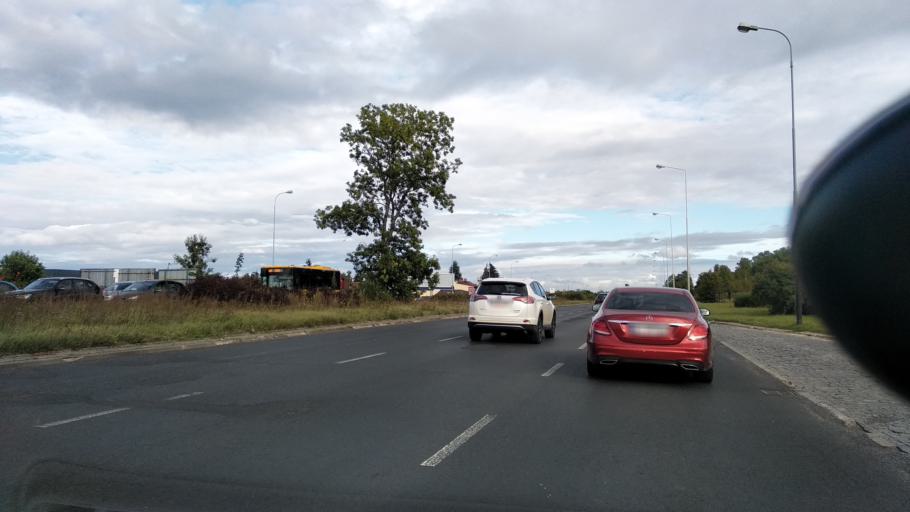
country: PL
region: Lodz Voivodeship
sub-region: Powiat lodzki wschodni
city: Andrespol
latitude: 51.7536
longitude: 19.5756
